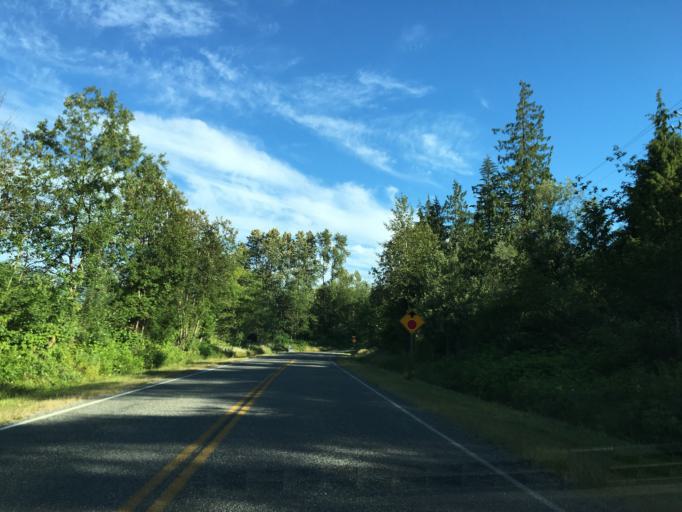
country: US
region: Washington
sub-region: Whatcom County
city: Sudden Valley
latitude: 48.6494
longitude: -122.3678
